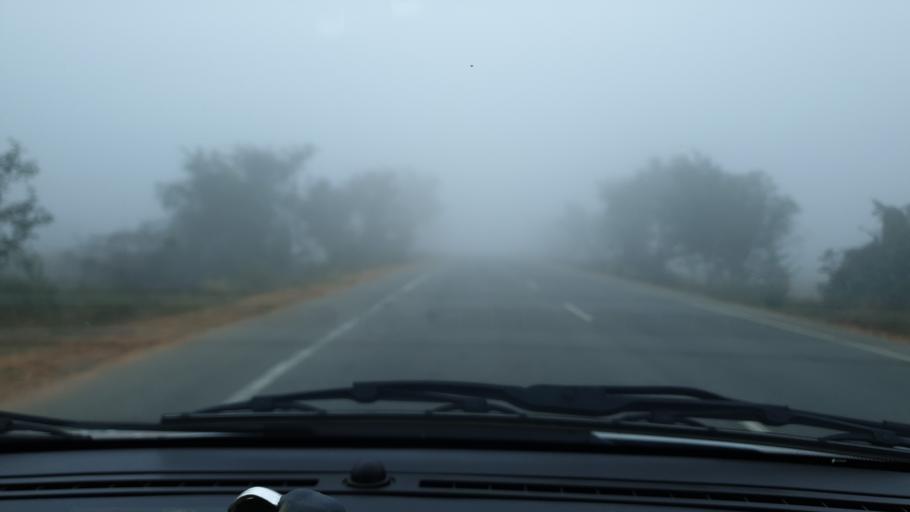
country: IN
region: Telangana
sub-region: Mahbubnagar
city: Nagar Karnul
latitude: 16.6784
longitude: 78.5279
